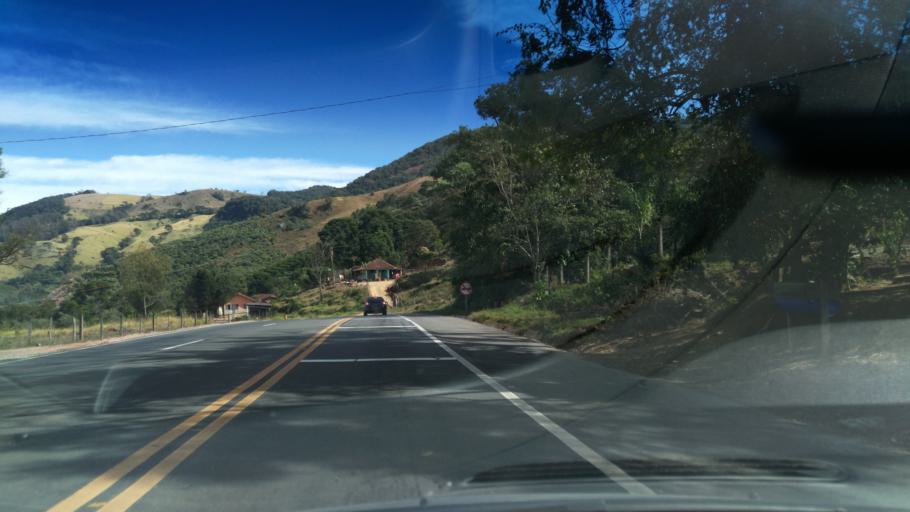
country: BR
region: Minas Gerais
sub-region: Borda Da Mata
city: Borda da Mata
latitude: -22.1336
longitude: -46.1745
